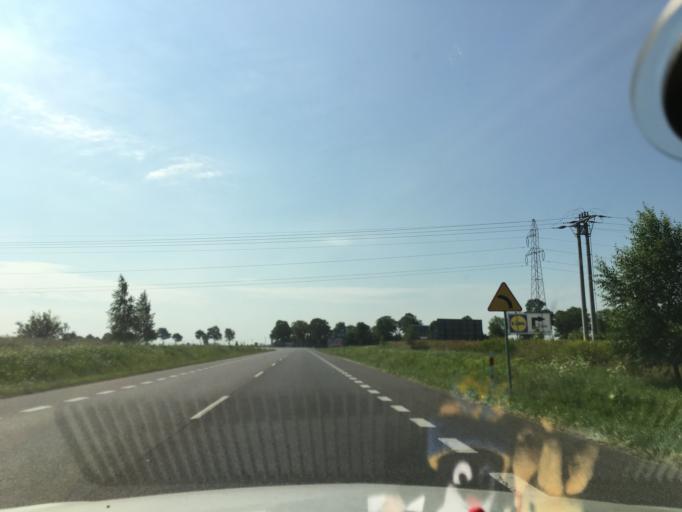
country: PL
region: West Pomeranian Voivodeship
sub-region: Powiat kamienski
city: Kamien Pomorski
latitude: 53.9593
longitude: 14.7921
